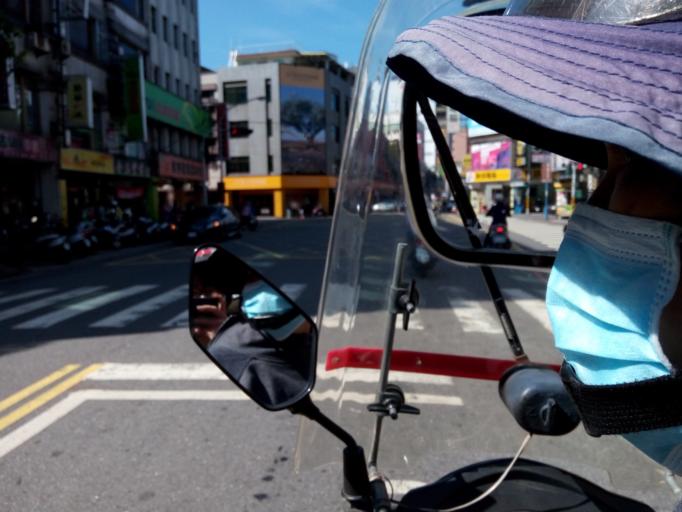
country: TW
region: Taiwan
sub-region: Yilan
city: Yilan
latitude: 24.6781
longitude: 121.7726
